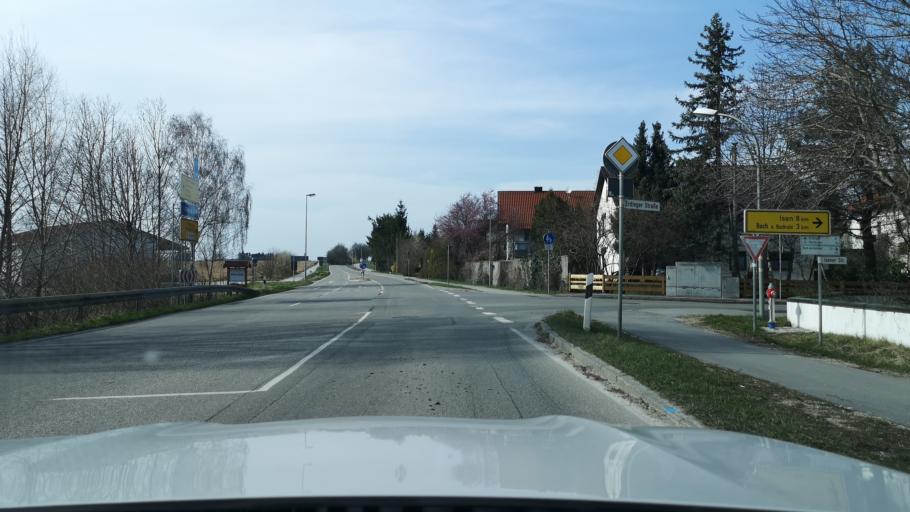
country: DE
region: Bavaria
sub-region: Upper Bavaria
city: Pastetten
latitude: 48.2069
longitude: 11.9592
